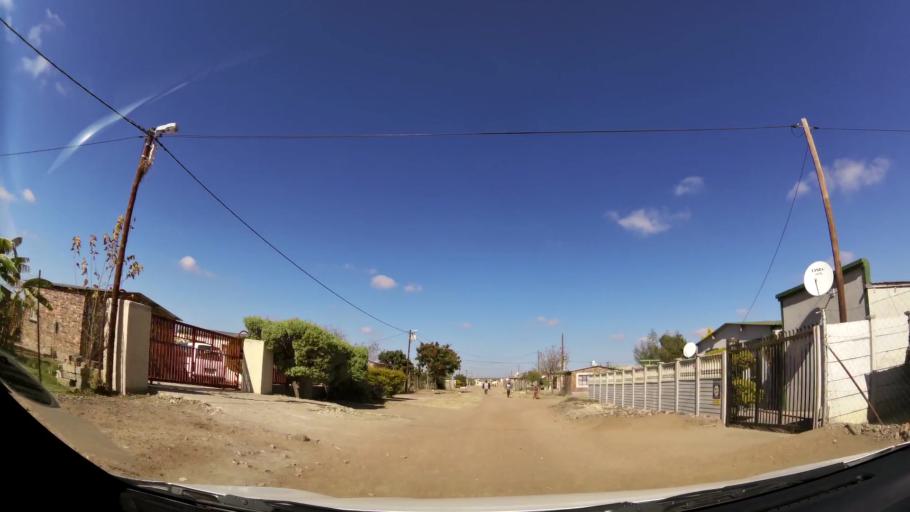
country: ZA
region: Limpopo
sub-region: Capricorn District Municipality
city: Polokwane
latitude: -23.8581
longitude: 29.3985
